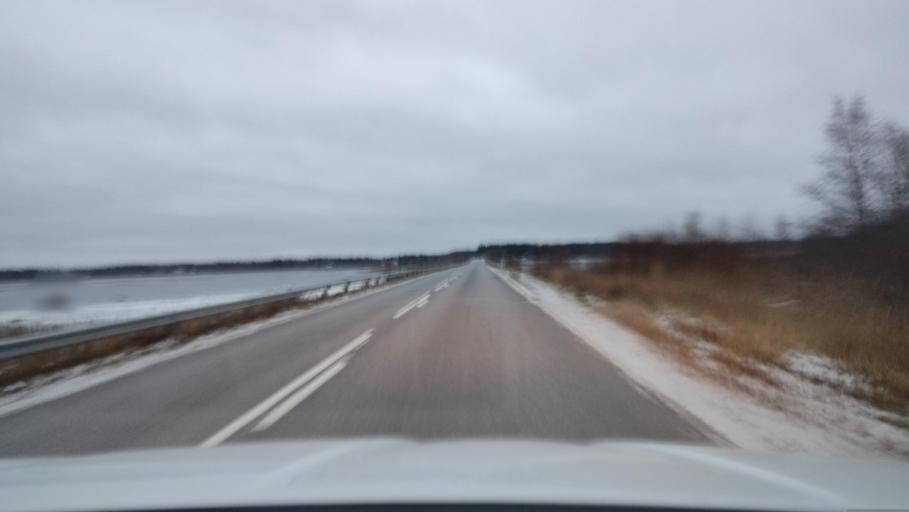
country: FI
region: Ostrobothnia
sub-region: Vaasa
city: Replot
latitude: 63.2781
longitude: 21.3417
